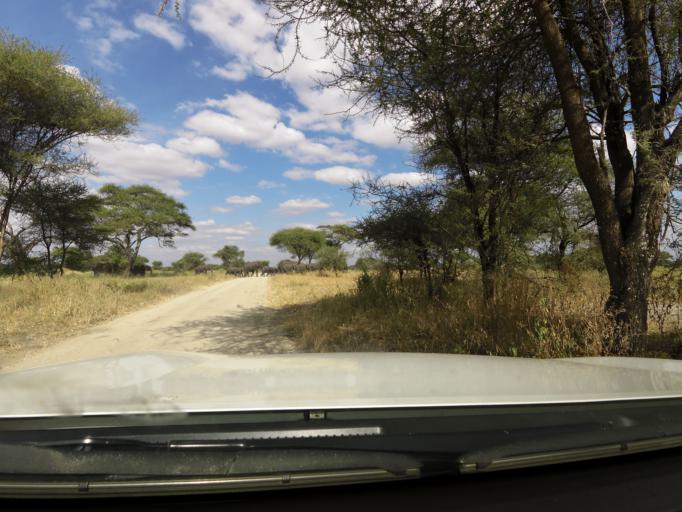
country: TZ
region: Manyara
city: Magugu
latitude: -3.7682
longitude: 35.9673
